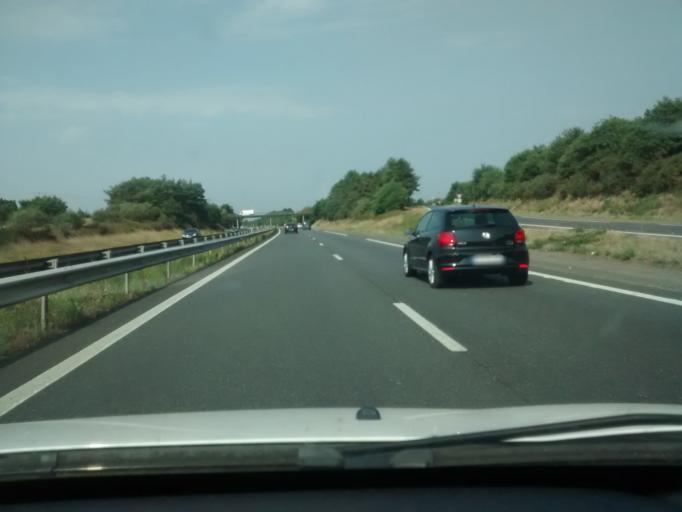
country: FR
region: Pays de la Loire
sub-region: Departement de la Loire-Atlantique
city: Prinquiau
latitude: 47.3573
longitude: -2.0017
